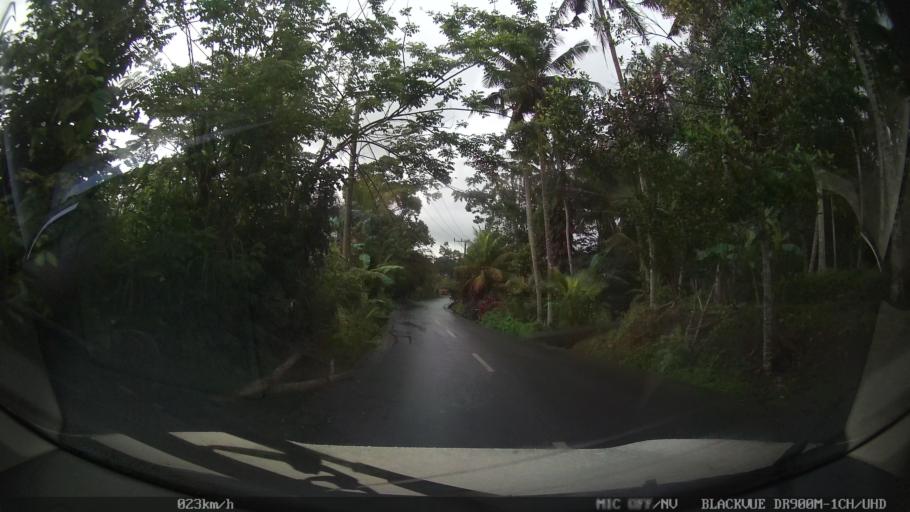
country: ID
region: Bali
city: Banjar Tengah
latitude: -8.5034
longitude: 115.1882
